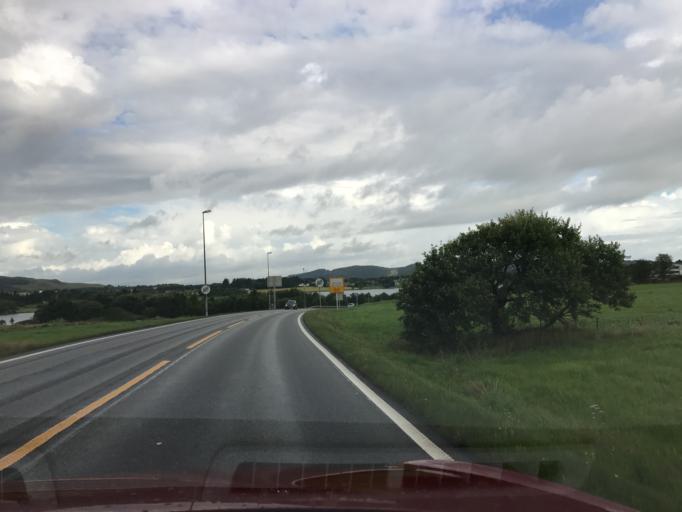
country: NO
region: Rogaland
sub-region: Rennesoy
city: Vikevag
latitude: 59.0662
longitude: 5.6743
